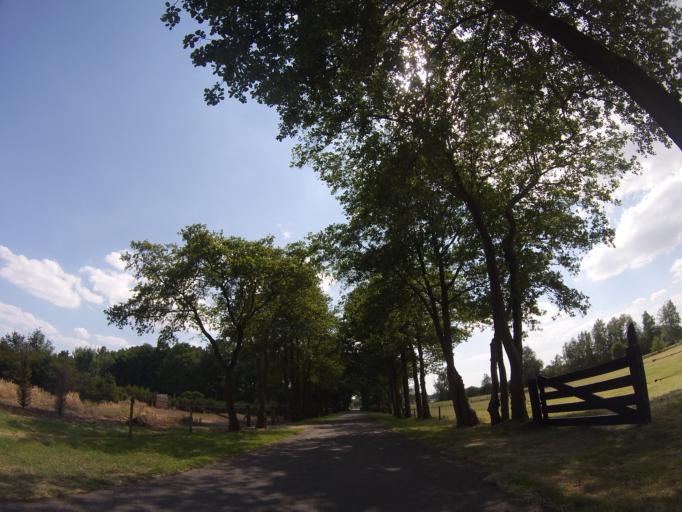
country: NL
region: Gelderland
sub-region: Gemeente Barneveld
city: Voorthuizen
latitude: 52.1775
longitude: 5.6270
